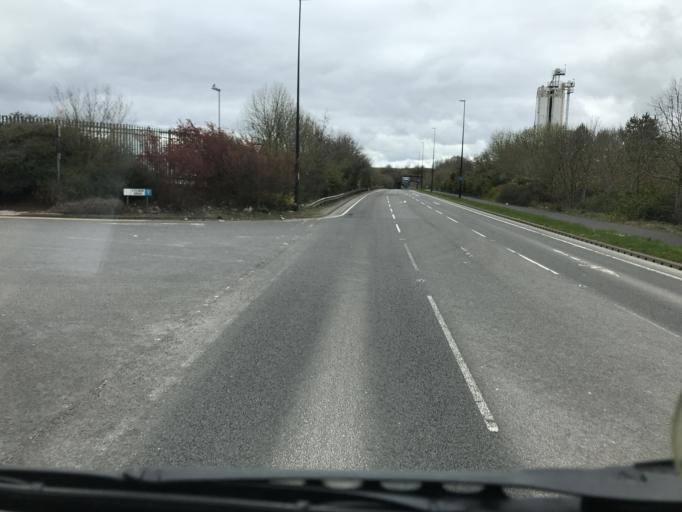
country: GB
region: England
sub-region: Trafford
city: Partington
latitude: 53.4280
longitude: -2.4263
